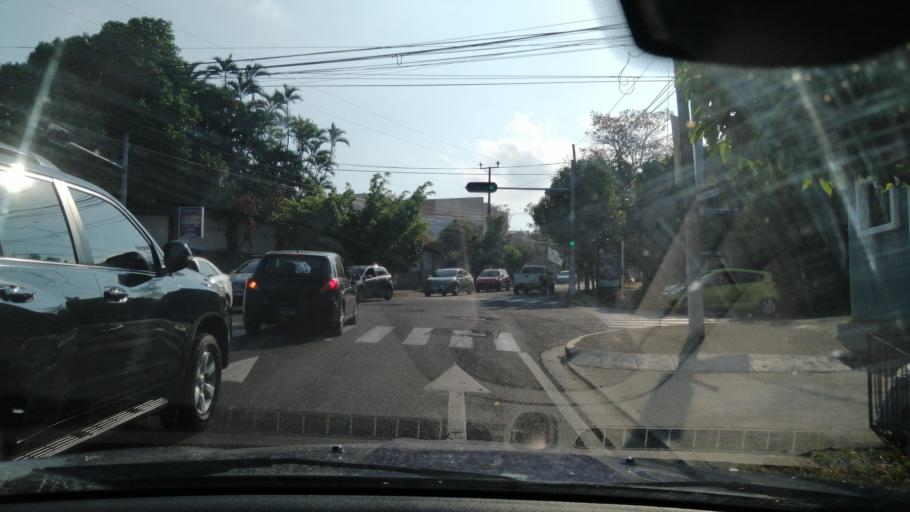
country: SV
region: La Libertad
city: Antiguo Cuscatlan
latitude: 13.6992
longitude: -89.2418
